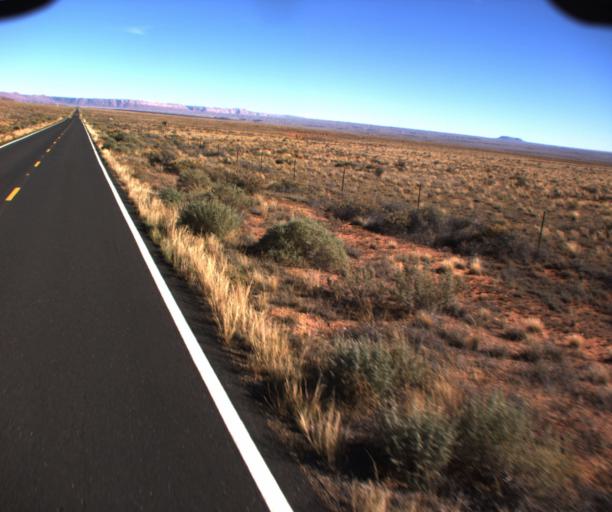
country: US
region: Arizona
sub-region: Coconino County
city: Page
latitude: 36.7057
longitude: -111.9506
